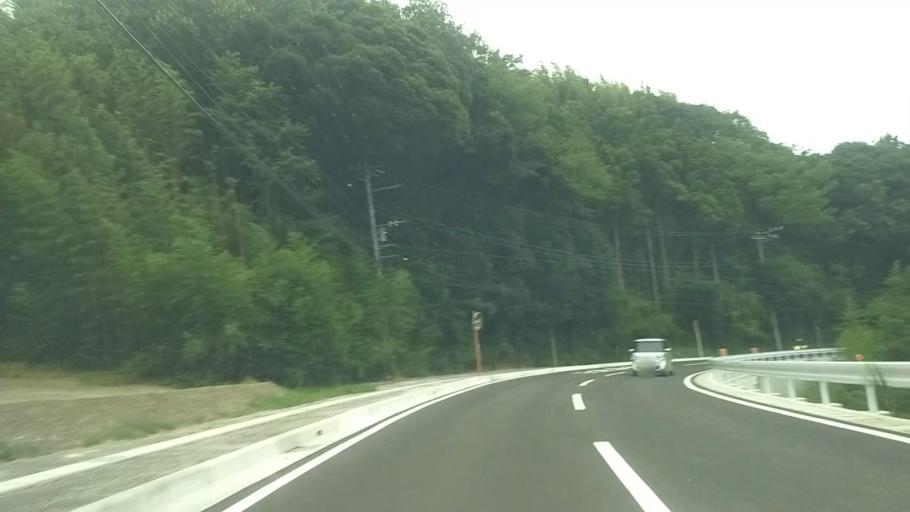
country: JP
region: Chiba
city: Kawaguchi
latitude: 35.2282
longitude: 140.0160
